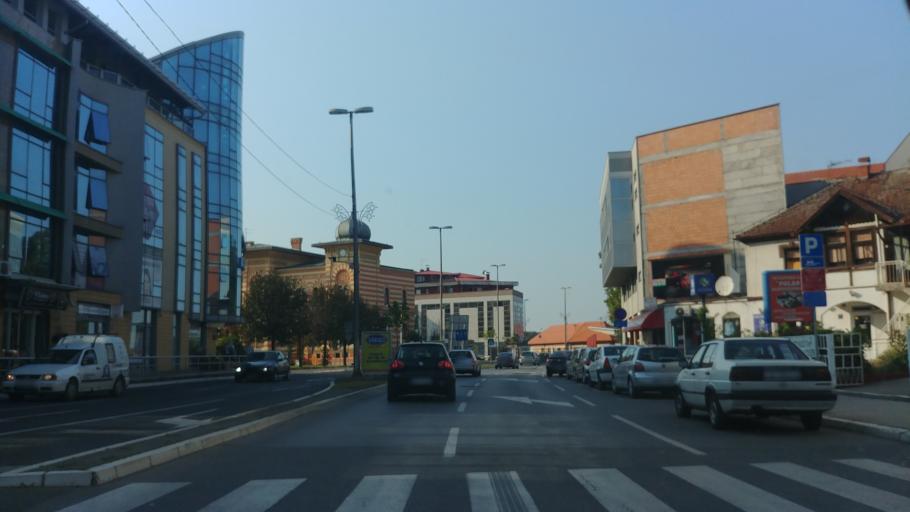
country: BA
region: Brcko
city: Brcko
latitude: 44.8773
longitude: 18.8106
